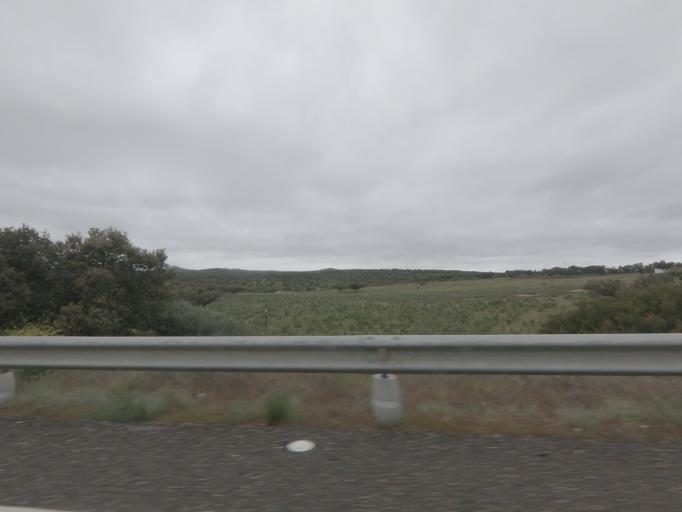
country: ES
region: Extremadura
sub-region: Provincia de Badajoz
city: La Roca de la Sierra
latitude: 39.1278
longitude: -6.6657
